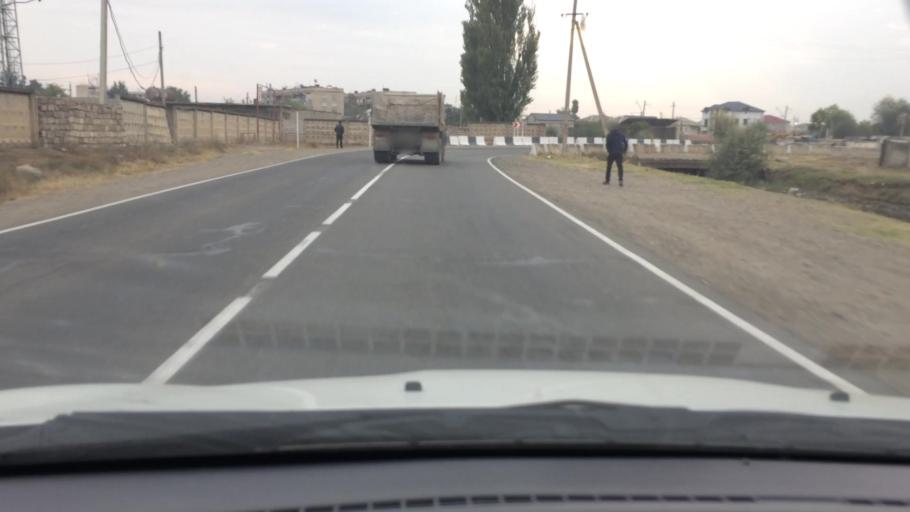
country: GE
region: Kvemo Kartli
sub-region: Marneuli
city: Marneuli
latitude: 41.4769
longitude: 44.8020
